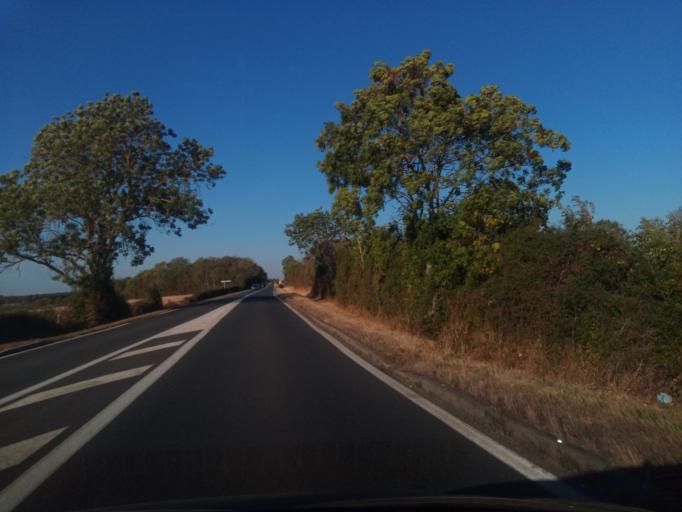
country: FR
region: Poitou-Charentes
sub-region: Departement de la Vienne
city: Lussac-les-Chateaux
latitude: 46.4049
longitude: 0.7850
